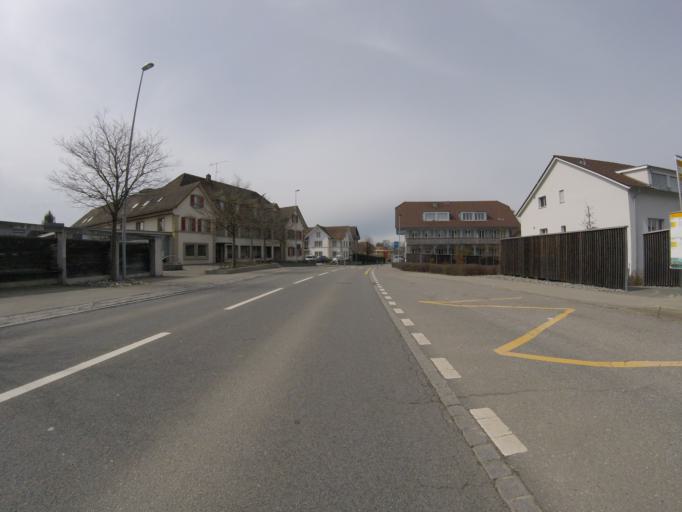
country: CH
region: Fribourg
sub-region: Sense District
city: Dudingen
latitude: 46.8935
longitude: 7.1748
